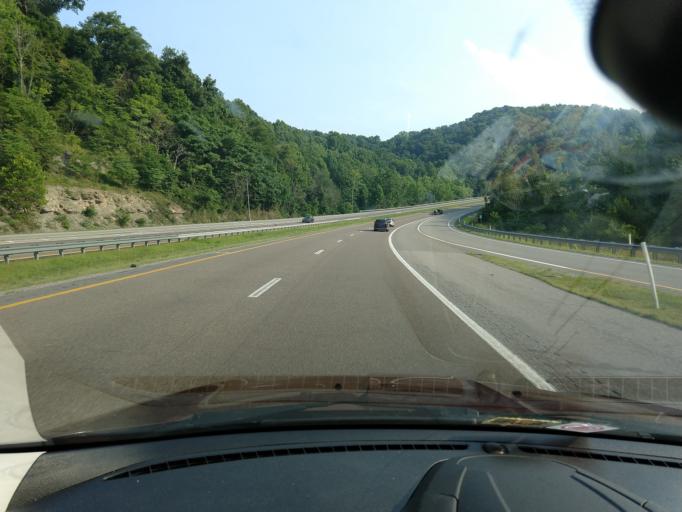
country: US
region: West Virginia
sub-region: Kanawha County
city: Charleston
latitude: 38.4151
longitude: -81.6321
